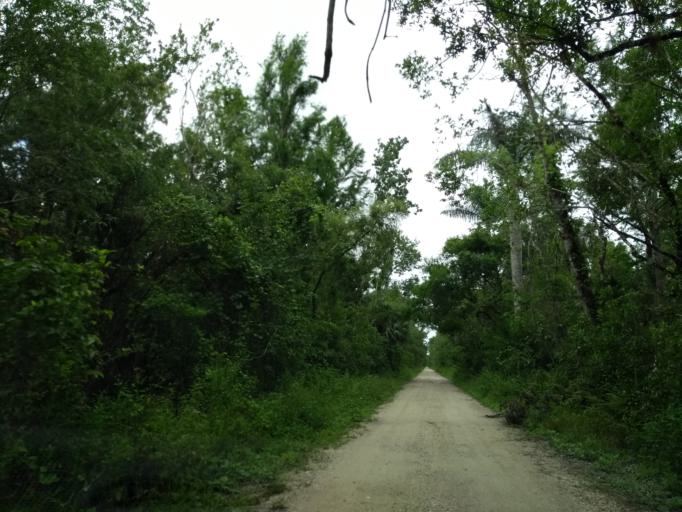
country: US
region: Florida
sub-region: Collier County
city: Lely Resort
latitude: 26.0022
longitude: -81.4112
